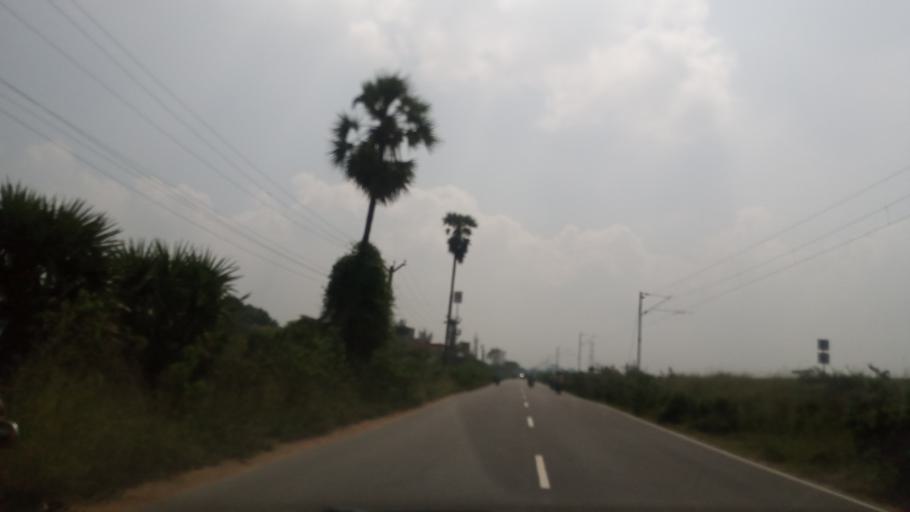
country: IN
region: Tamil Nadu
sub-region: Kancheepuram
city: Kanchipuram
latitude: 12.8930
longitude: 79.6861
